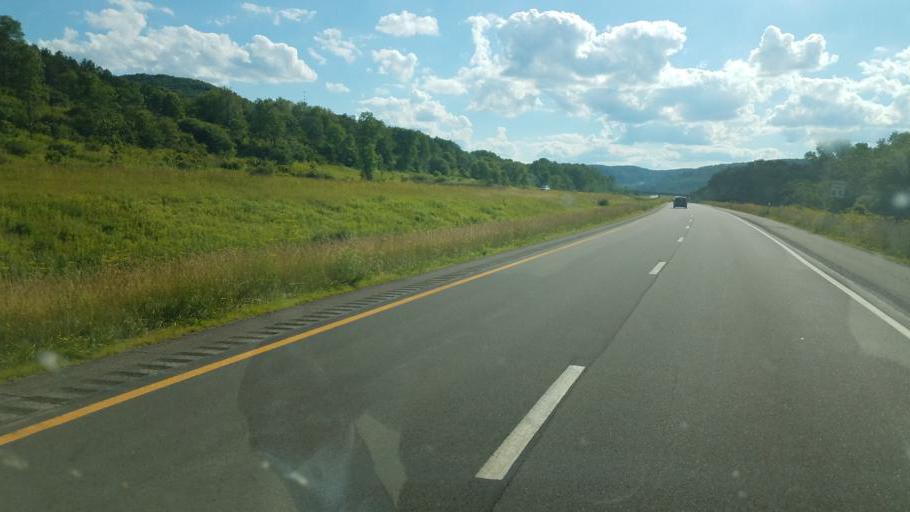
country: US
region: New York
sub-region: Allegany County
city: Cuba
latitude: 42.1806
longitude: -78.3620
